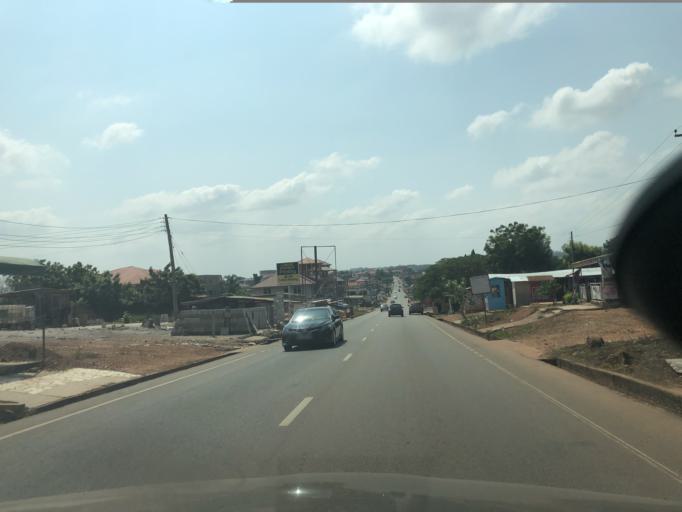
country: GH
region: Greater Accra
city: Medina Estates
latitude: 5.6807
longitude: -0.1927
